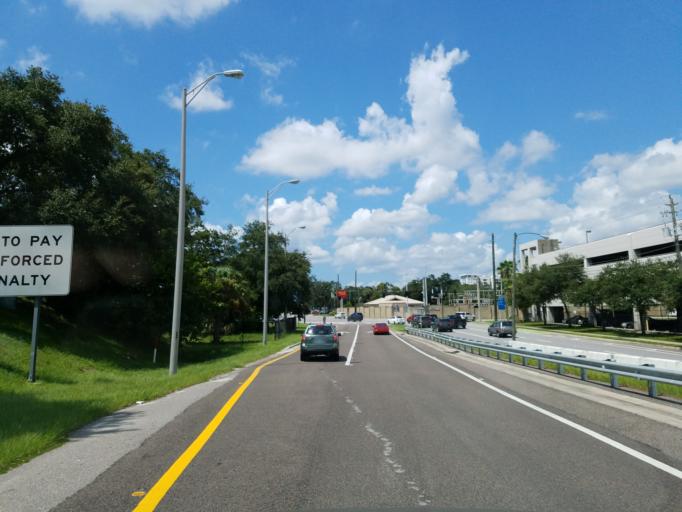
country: US
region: Florida
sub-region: Hillsborough County
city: Tampa
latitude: 27.9432
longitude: -82.4616
